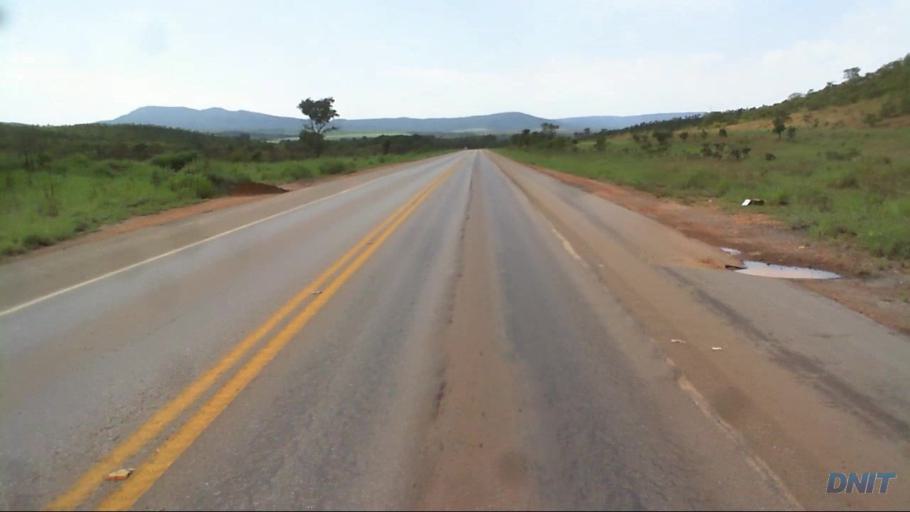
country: BR
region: Goias
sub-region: Barro Alto
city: Barro Alto
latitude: -15.1720
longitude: -48.7957
